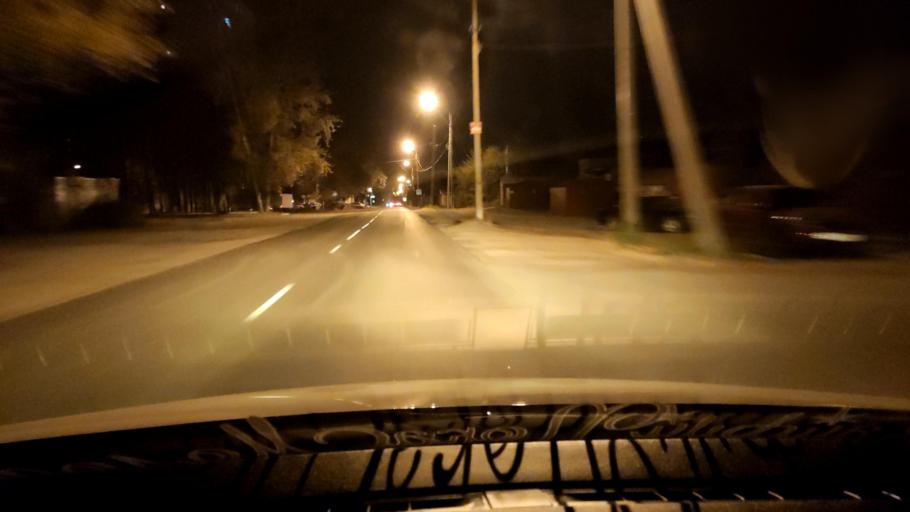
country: RU
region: Voronezj
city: Pridonskoy
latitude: 51.6888
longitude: 39.0807
